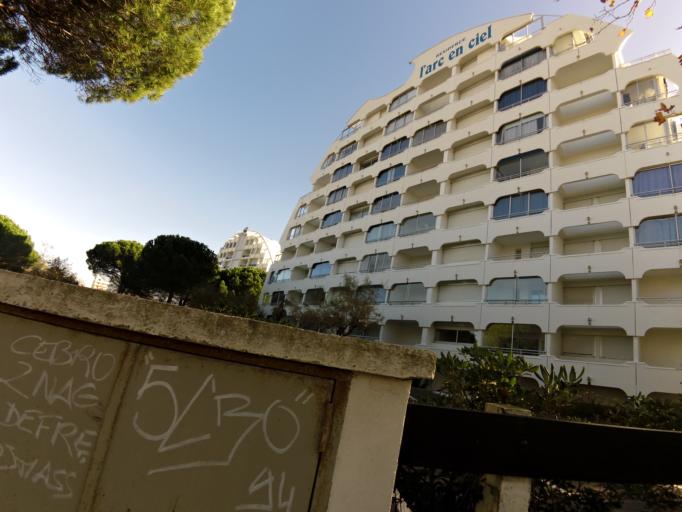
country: FR
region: Languedoc-Roussillon
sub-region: Departement de l'Herault
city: La Grande-Motte
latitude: 43.5601
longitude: 4.0633
